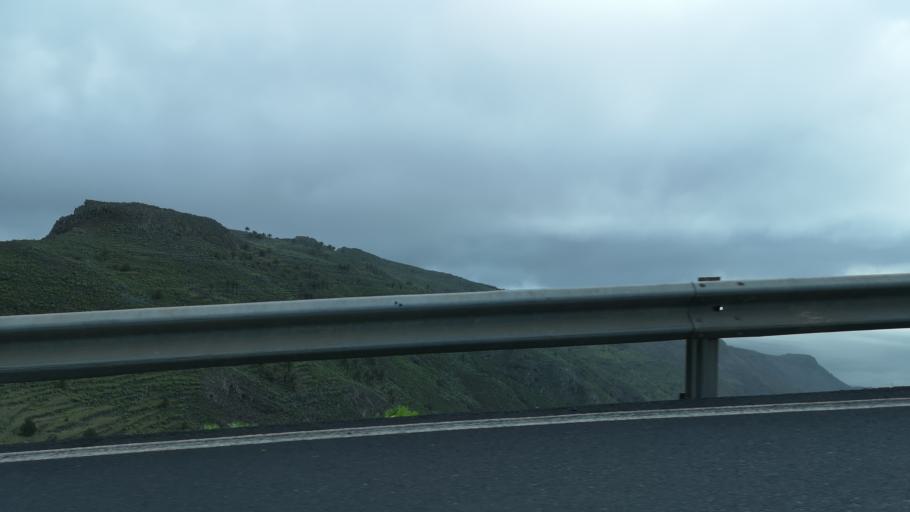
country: ES
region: Canary Islands
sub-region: Provincia de Santa Cruz de Tenerife
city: San Sebastian de la Gomera
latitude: 28.0998
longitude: -17.1716
